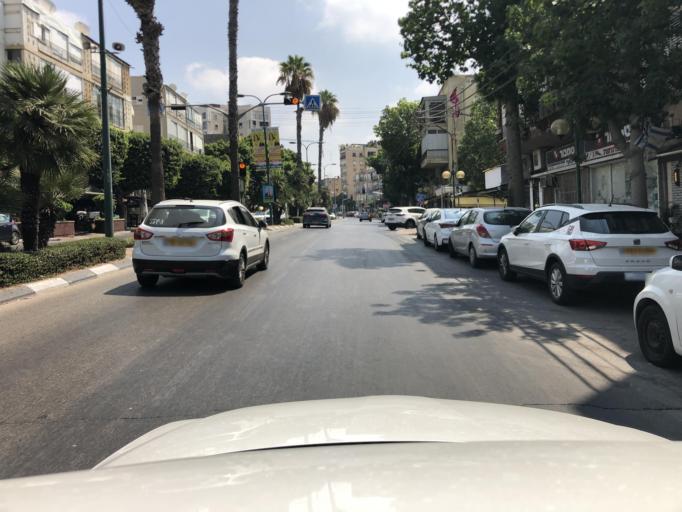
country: IL
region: Tel Aviv
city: Giv`atayim
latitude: 32.0751
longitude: 34.8070
